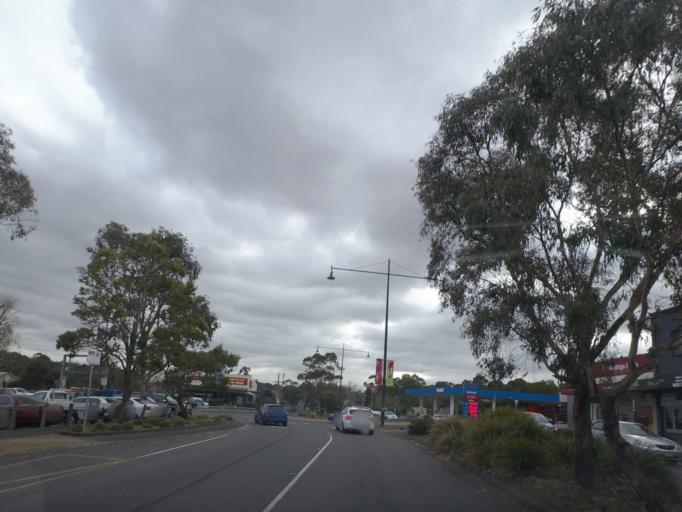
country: AU
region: Victoria
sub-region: Nillumbik
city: Eltham North
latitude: -37.7127
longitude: 145.1488
